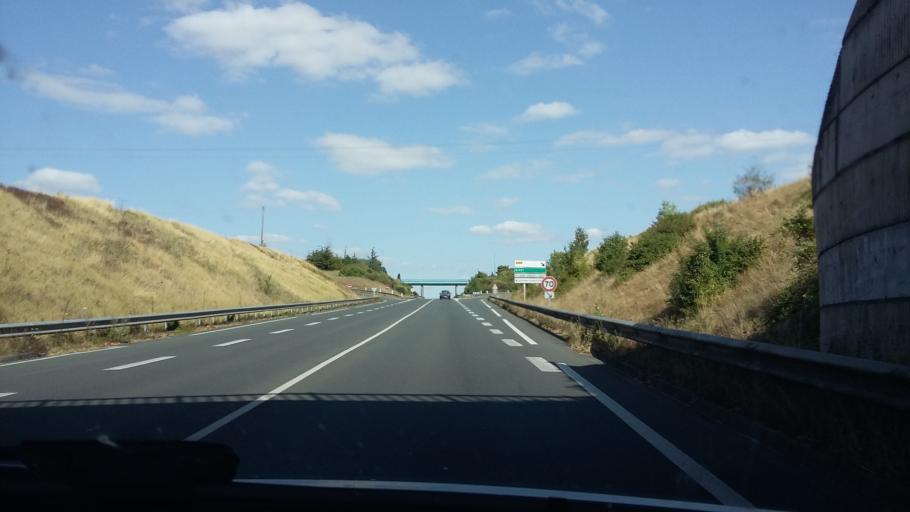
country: FR
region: Poitou-Charentes
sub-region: Departement de la Charente-Maritime
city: Saint-Jean-d'Angely
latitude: 45.9559
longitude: -0.5204
